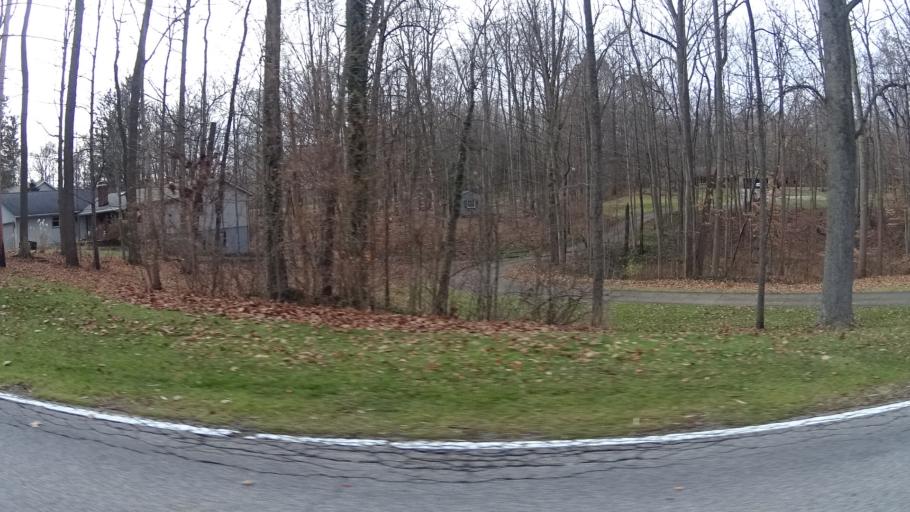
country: US
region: Ohio
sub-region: Lorain County
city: Eaton Estates
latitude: 41.2824
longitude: -81.9322
